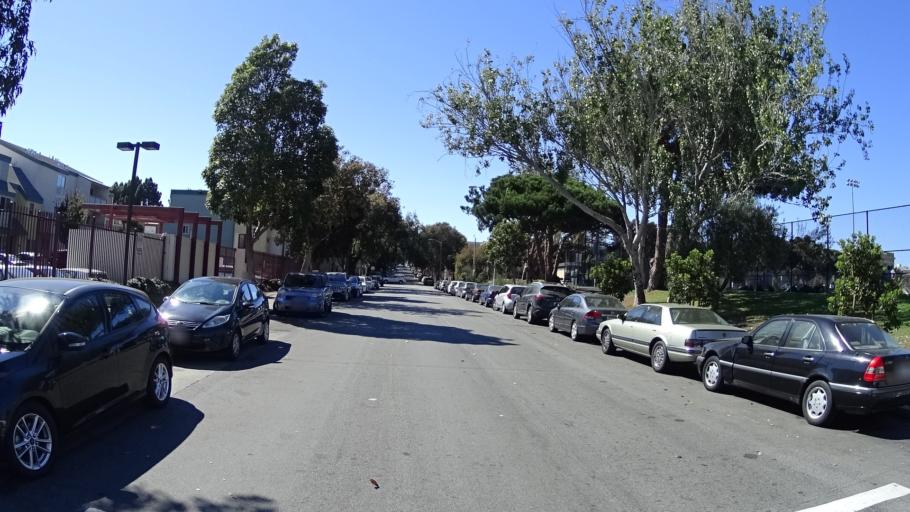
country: US
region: California
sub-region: San Francisco County
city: San Francisco
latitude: 37.7821
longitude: -122.4348
